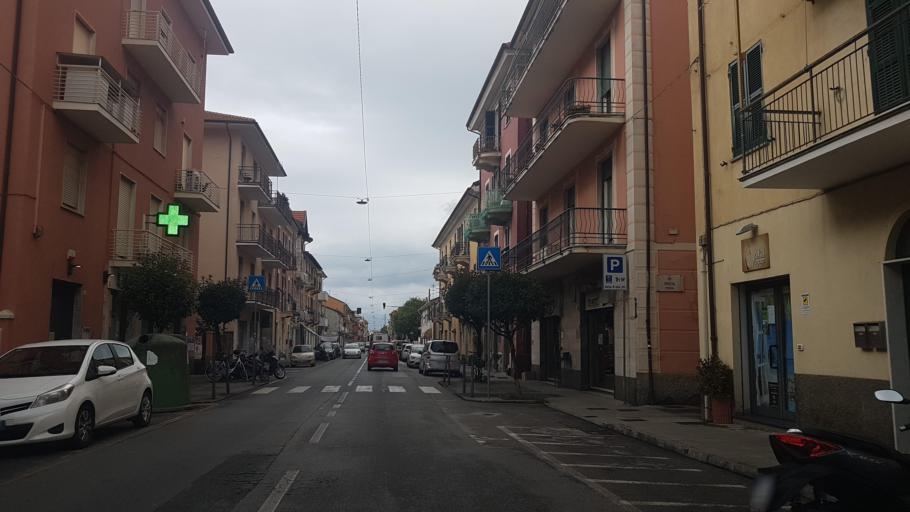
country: IT
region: Liguria
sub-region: Provincia di Genova
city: Sestri Levante
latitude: 44.2720
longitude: 9.4116
